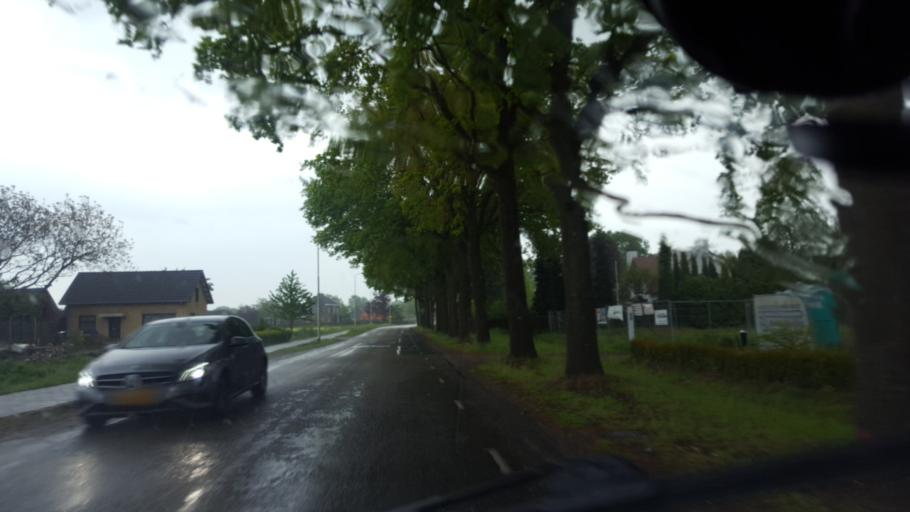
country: NL
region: North Brabant
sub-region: Gemeente Someren
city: Someren
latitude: 51.3926
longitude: 5.6966
